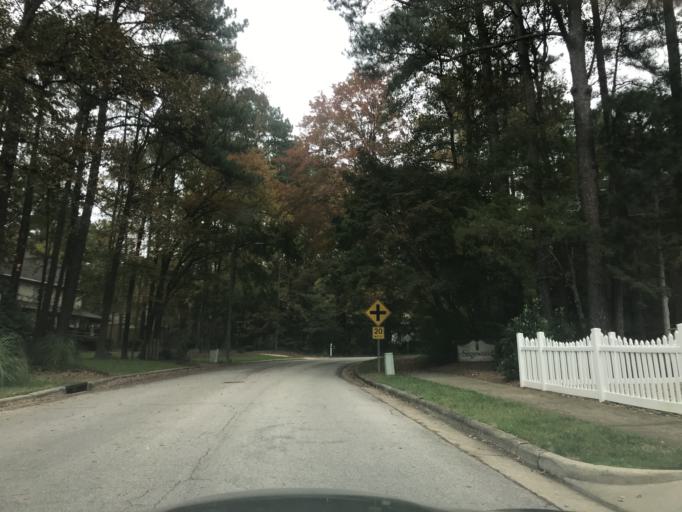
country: US
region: North Carolina
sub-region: Wake County
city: West Raleigh
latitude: 35.8912
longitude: -78.6353
